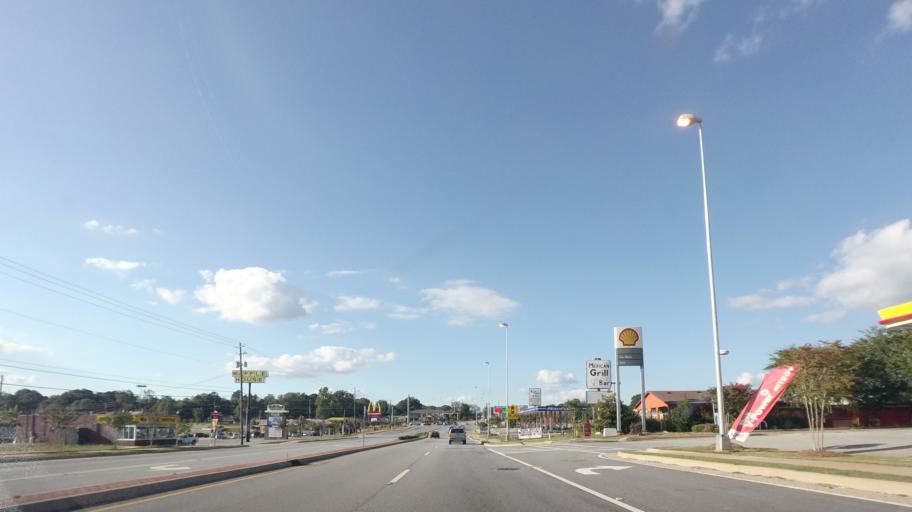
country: US
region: Georgia
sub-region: Upson County
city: Hannahs Mill
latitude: 32.9248
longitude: -84.3335
